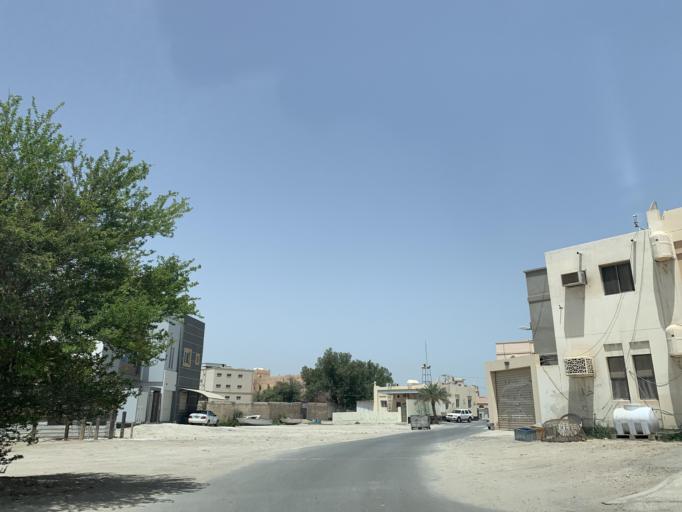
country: BH
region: Northern
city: Sitrah
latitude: 26.1718
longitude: 50.6095
